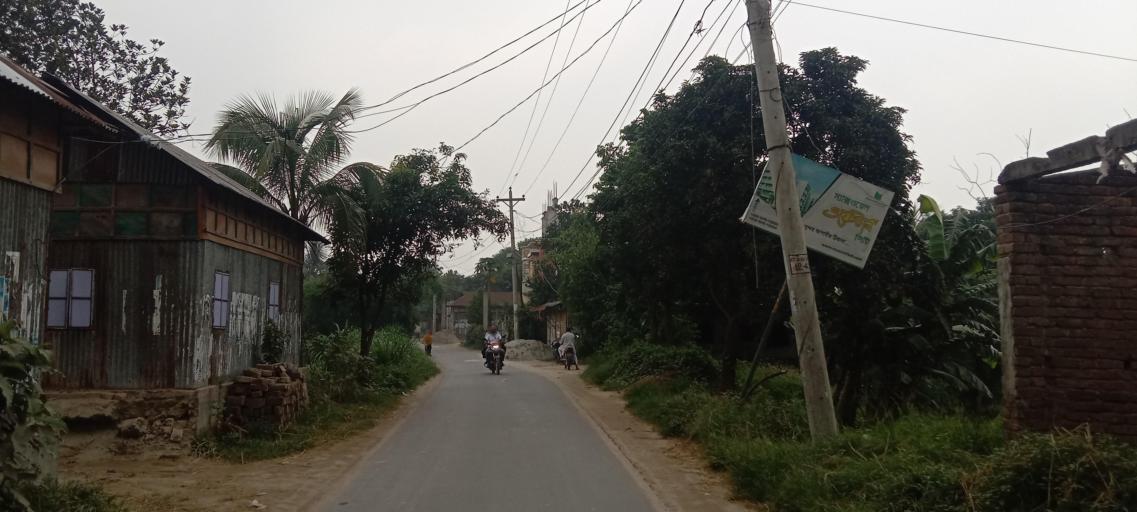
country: BD
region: Dhaka
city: Azimpur
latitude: 23.7405
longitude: 90.3130
